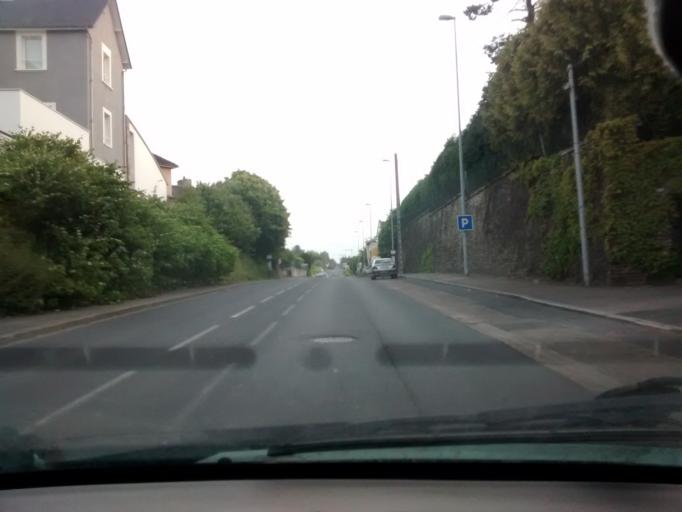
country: FR
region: Lower Normandy
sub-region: Departement de la Manche
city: Agneaux
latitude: 49.1108
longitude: -1.1032
